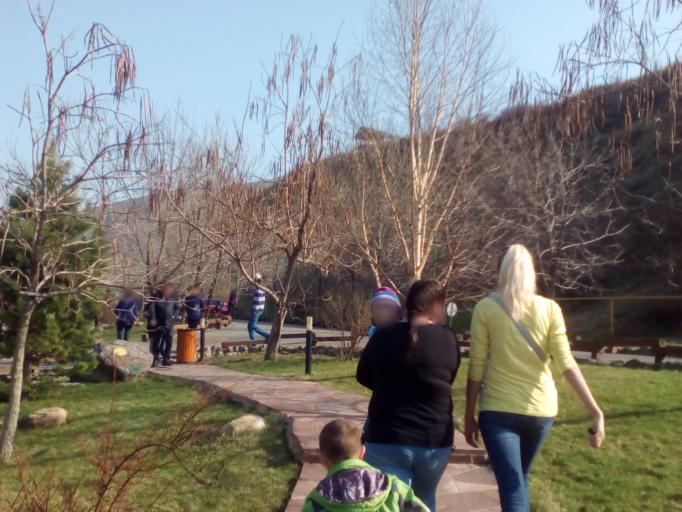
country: KZ
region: Almaty Oblysy
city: Burunday
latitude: 43.1532
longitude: 76.5688
